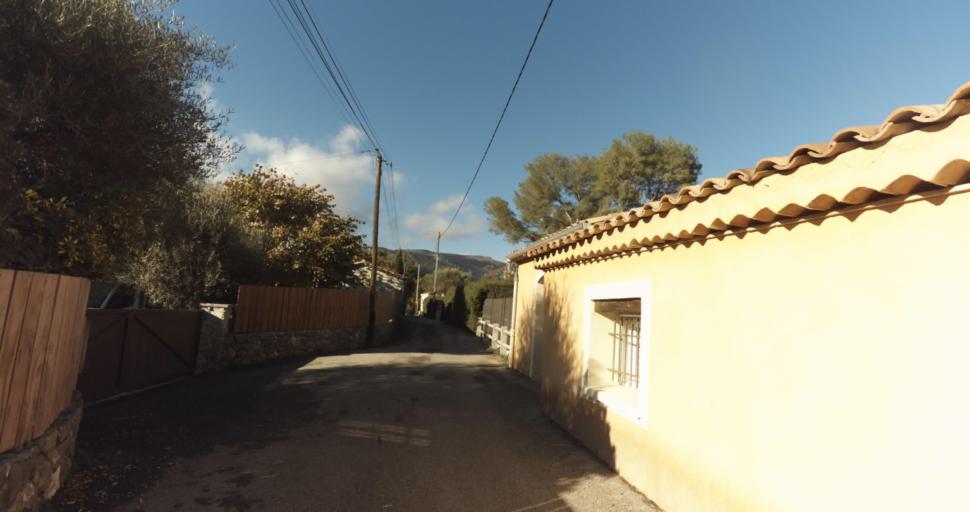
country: FR
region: Provence-Alpes-Cote d'Azur
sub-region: Departement des Alpes-Maritimes
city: La Gaude
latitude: 43.7142
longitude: 7.1357
